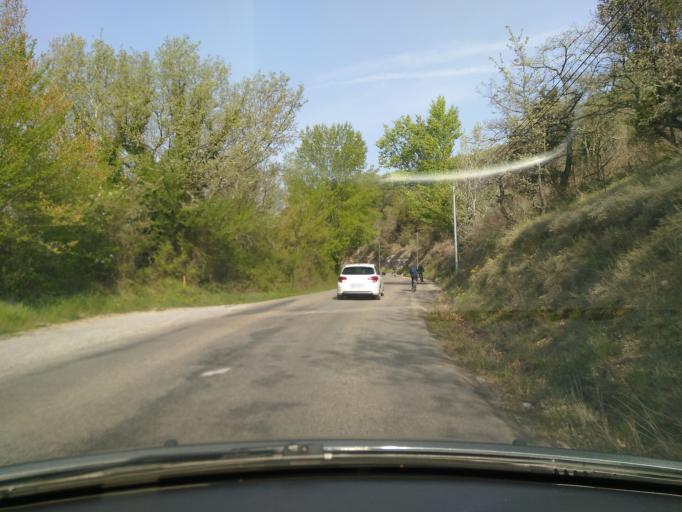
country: FR
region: Rhone-Alpes
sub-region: Departement de l'Ardeche
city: Ruoms
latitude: 44.4476
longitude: 4.3613
